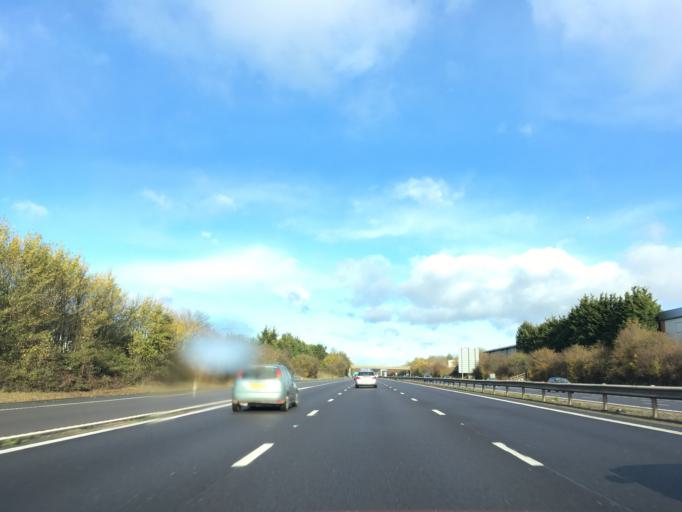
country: GB
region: England
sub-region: Worcestershire
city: Bredon
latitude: 51.9999
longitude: -2.1231
